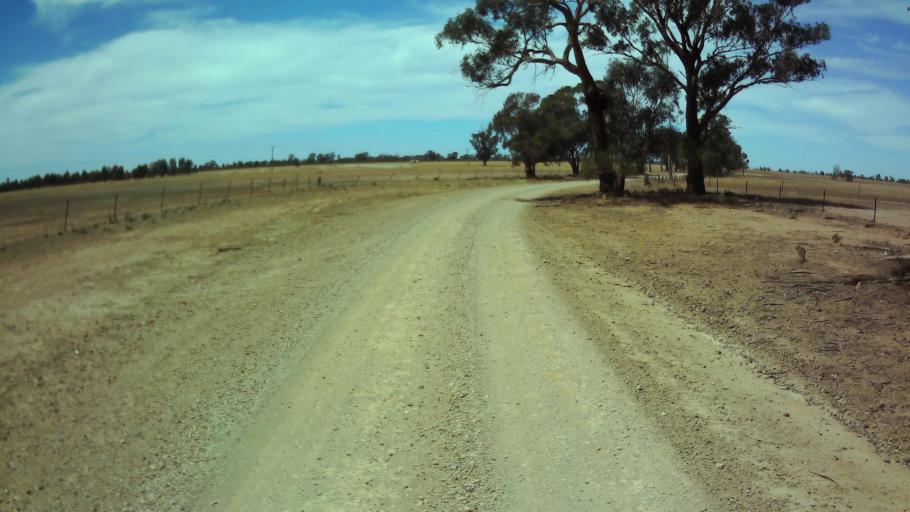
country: AU
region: New South Wales
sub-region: Weddin
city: Grenfell
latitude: -33.8647
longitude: 147.8071
